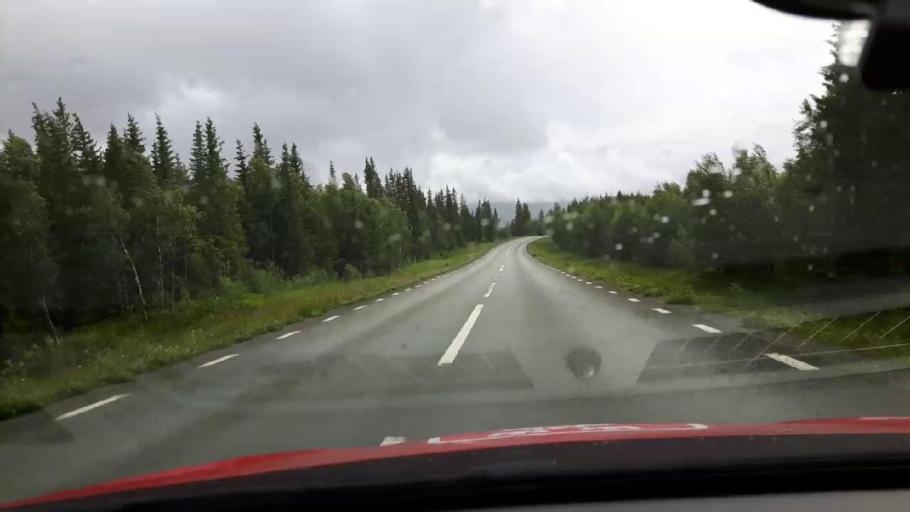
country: SE
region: Jaemtland
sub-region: Are Kommun
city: Are
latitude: 63.3029
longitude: 12.4230
